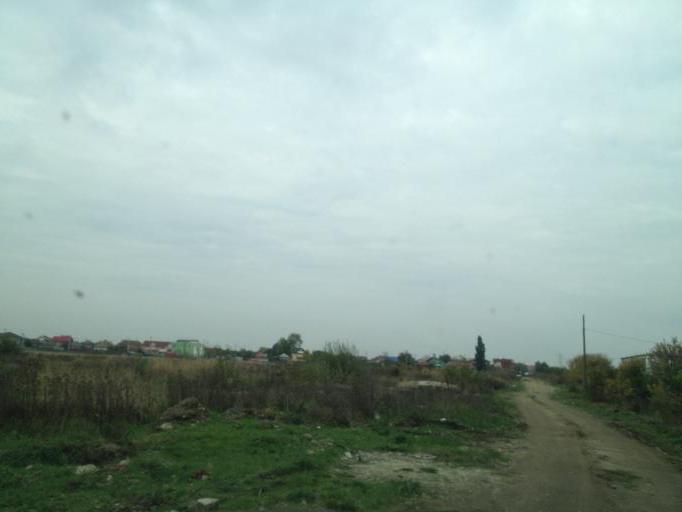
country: RO
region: Dolj
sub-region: Municipiul Craiova
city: Popoveni
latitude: 44.2916
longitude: 23.7910
